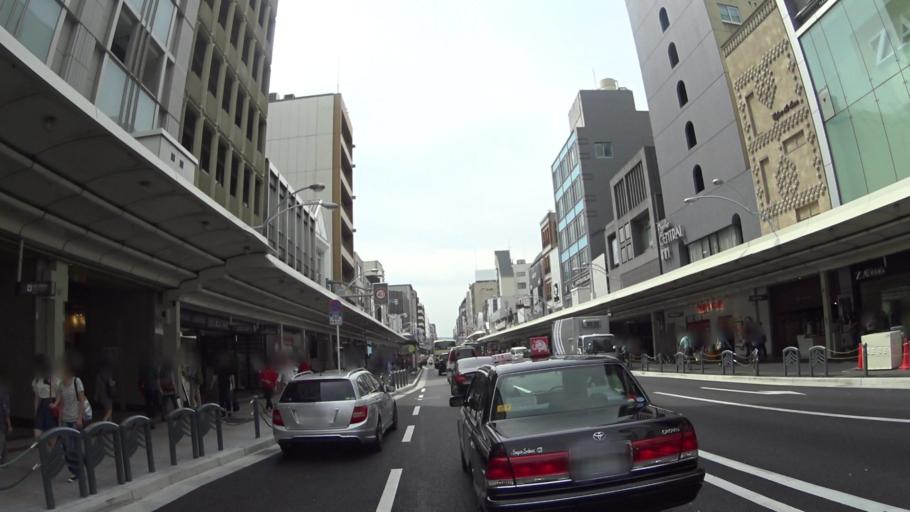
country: JP
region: Kyoto
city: Kyoto
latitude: 35.0037
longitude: 135.7688
